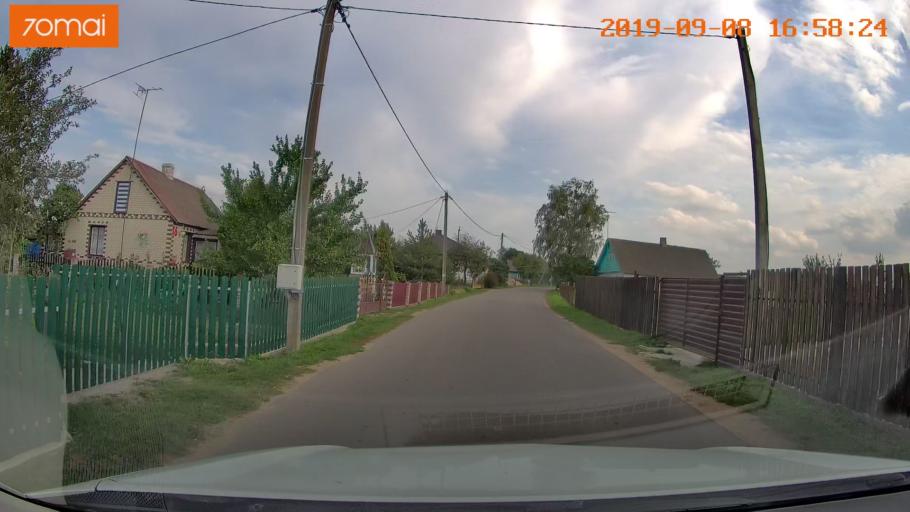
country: BY
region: Grodnenskaya
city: Hrodna
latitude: 53.7271
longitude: 23.9267
